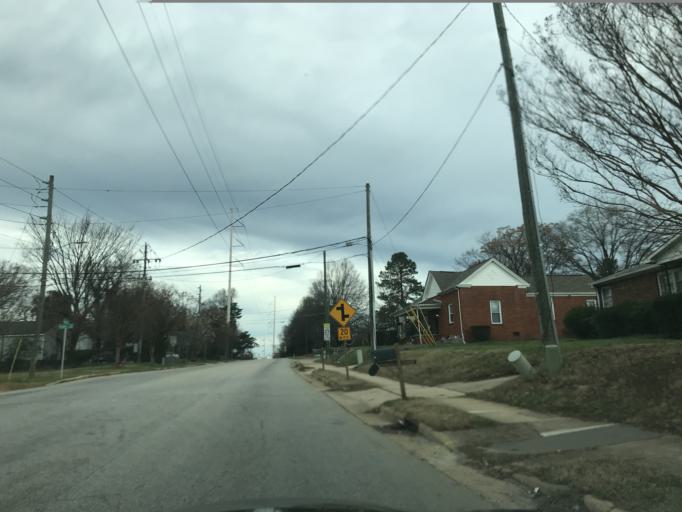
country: US
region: North Carolina
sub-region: Wake County
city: Raleigh
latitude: 35.7631
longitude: -78.6314
